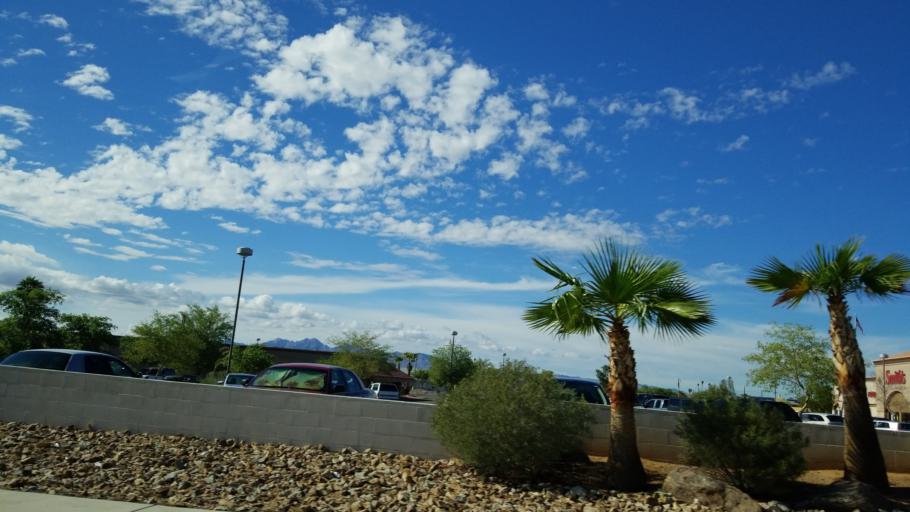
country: US
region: Arizona
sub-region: Mohave County
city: Lake Havasu City
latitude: 34.4763
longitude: -114.3217
